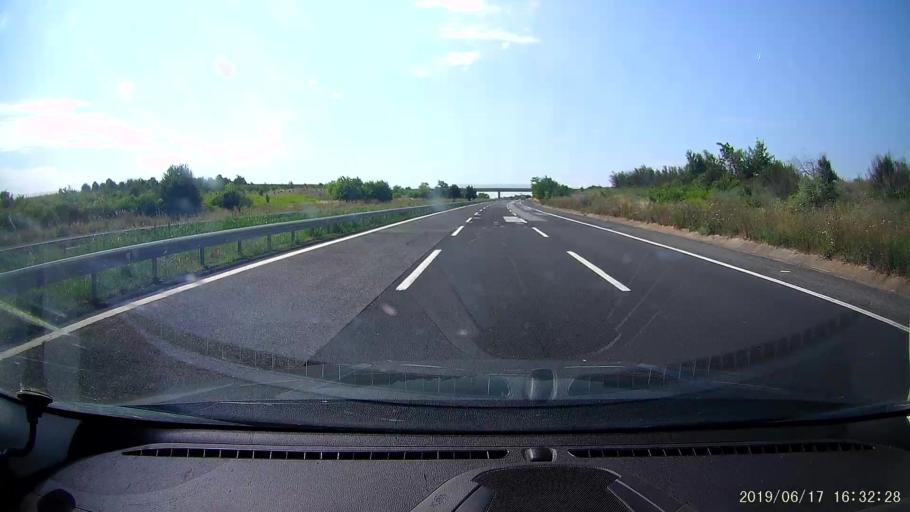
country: TR
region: Kirklareli
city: Buyukkaristiran
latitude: 41.3692
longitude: 27.5991
